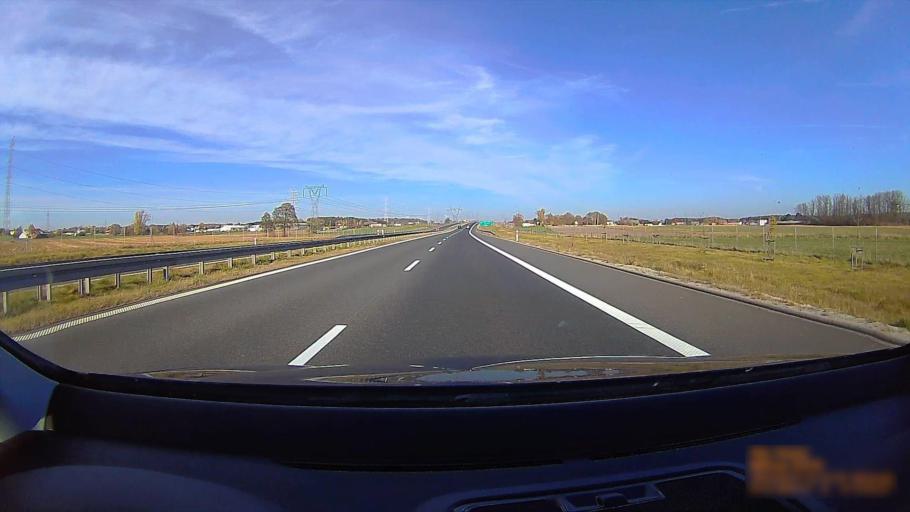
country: PL
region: Greater Poland Voivodeship
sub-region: Powiat ostrowski
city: Przygodzice
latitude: 51.5996
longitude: 17.8519
